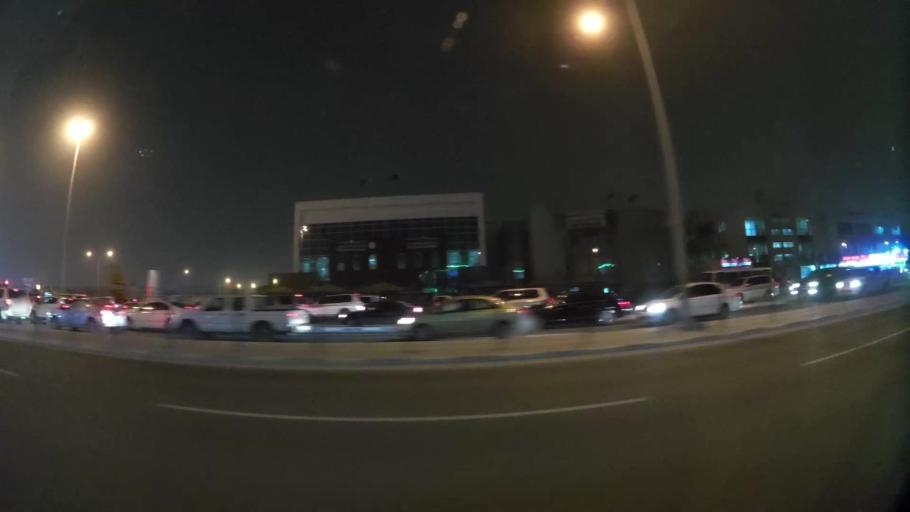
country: QA
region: Baladiyat ad Dawhah
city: Doha
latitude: 25.2298
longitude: 51.4883
